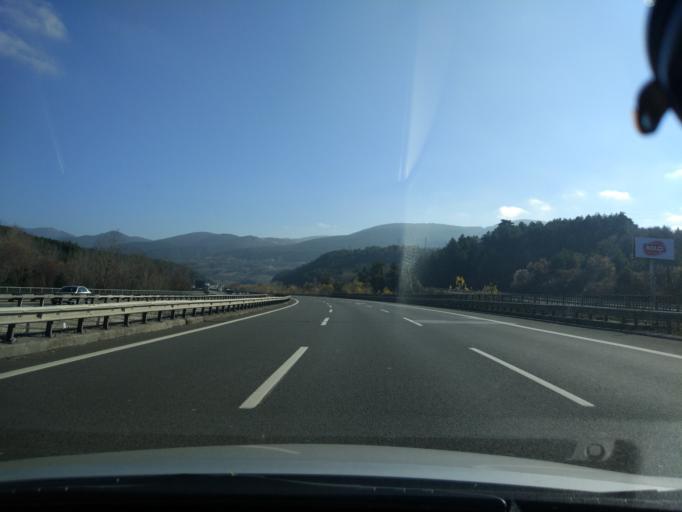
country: TR
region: Bolu
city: Bolu
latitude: 40.7418
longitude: 31.7853
